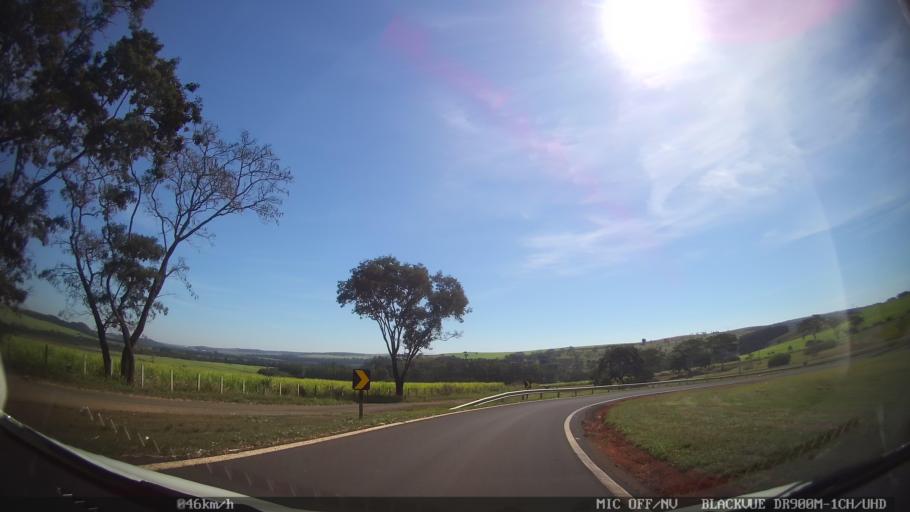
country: BR
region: Sao Paulo
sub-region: Santa Rita Do Passa Quatro
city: Santa Rita do Passa Quatro
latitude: -21.7567
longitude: -47.5653
